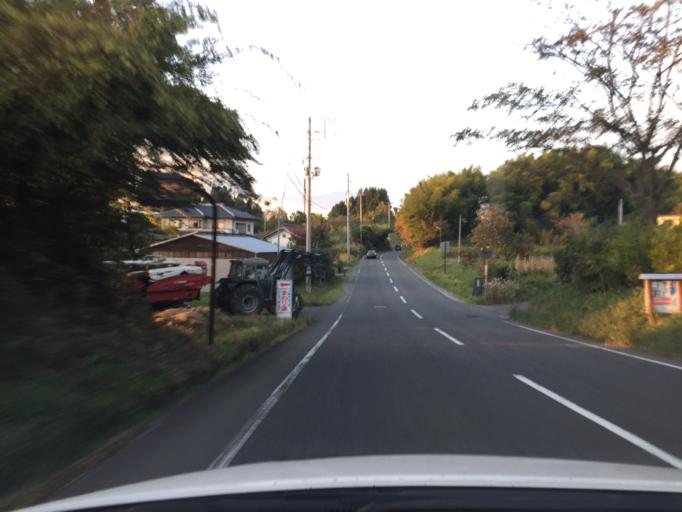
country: JP
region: Fukushima
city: Koriyama
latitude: 37.3615
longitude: 140.4481
